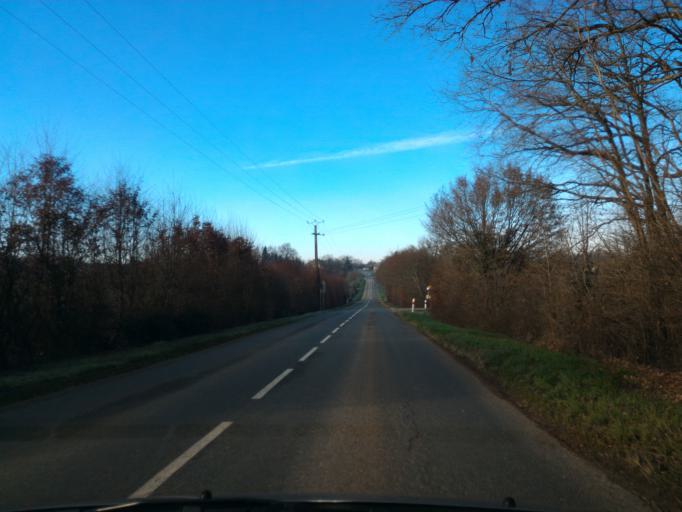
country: FR
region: Poitou-Charentes
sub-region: Departement de la Charente
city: Confolens
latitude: 46.0319
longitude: 0.5462
